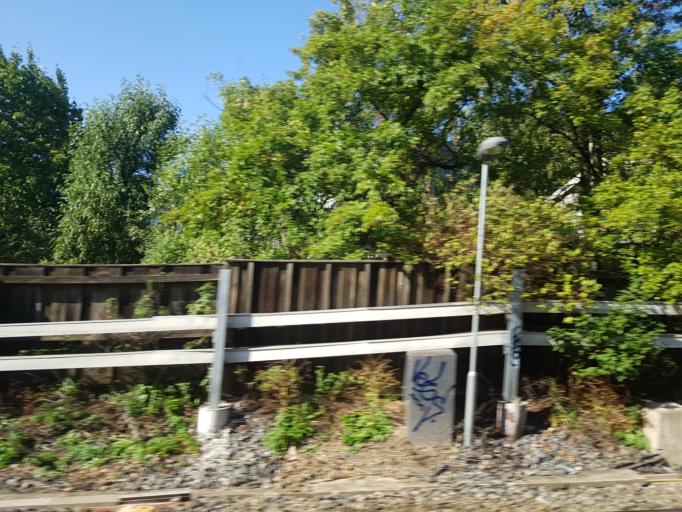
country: NO
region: Oslo
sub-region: Oslo
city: Sjolyststranda
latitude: 59.9196
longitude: 10.6613
